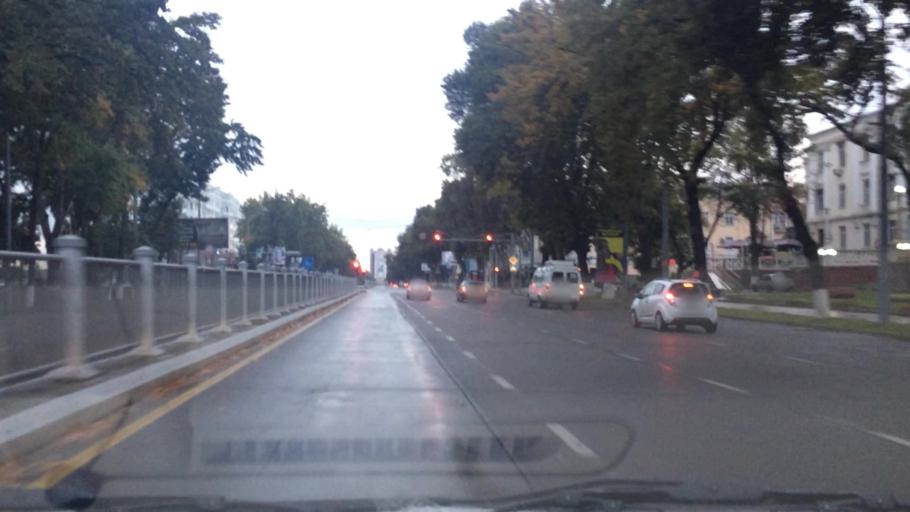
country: UZ
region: Toshkent Shahri
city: Tashkent
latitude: 41.3211
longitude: 69.2560
